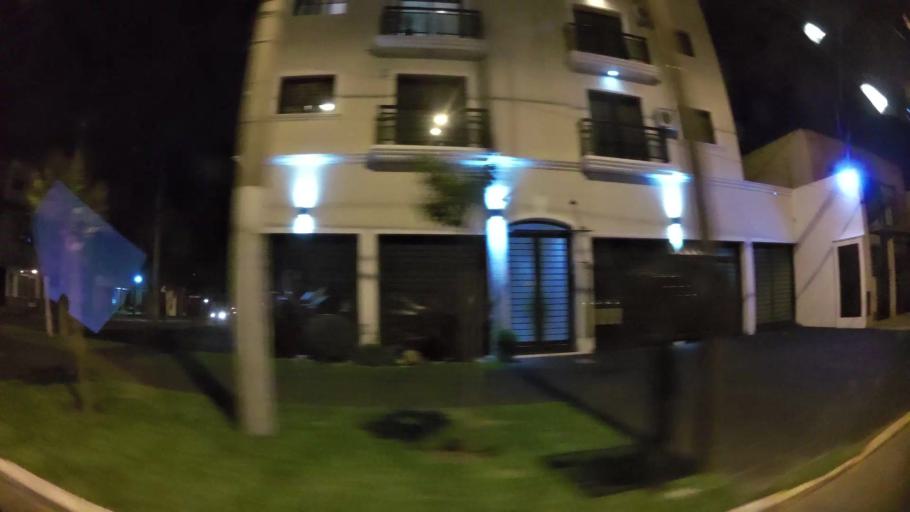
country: AR
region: Buenos Aires
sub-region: Partido de Quilmes
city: Quilmes
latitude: -34.7150
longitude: -58.2812
